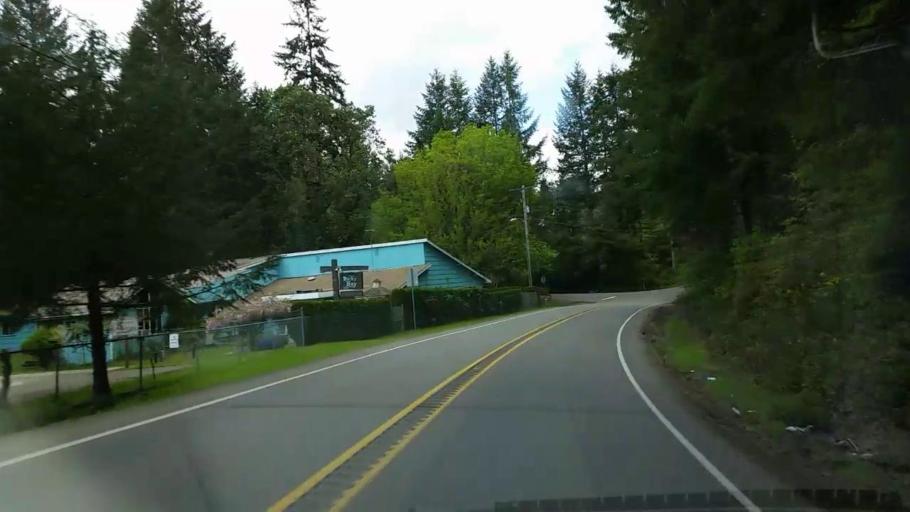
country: US
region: Washington
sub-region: Pierce County
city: Key Center
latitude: 47.3687
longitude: -122.7729
